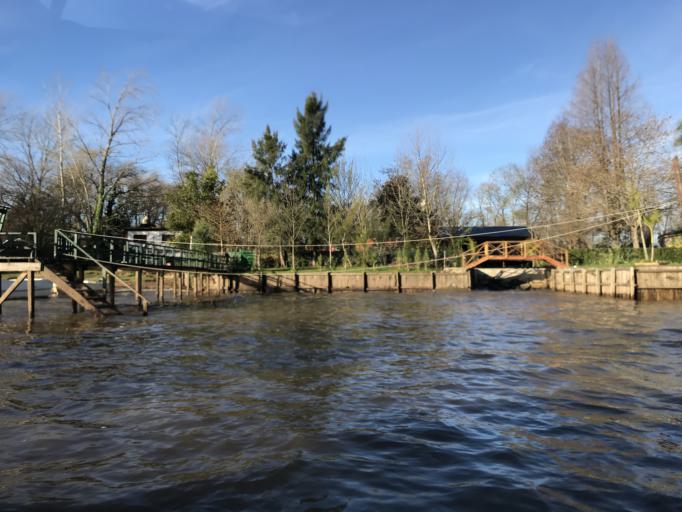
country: AR
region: Buenos Aires
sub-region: Partido de Tigre
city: Tigre
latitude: -34.4010
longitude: -58.5945
